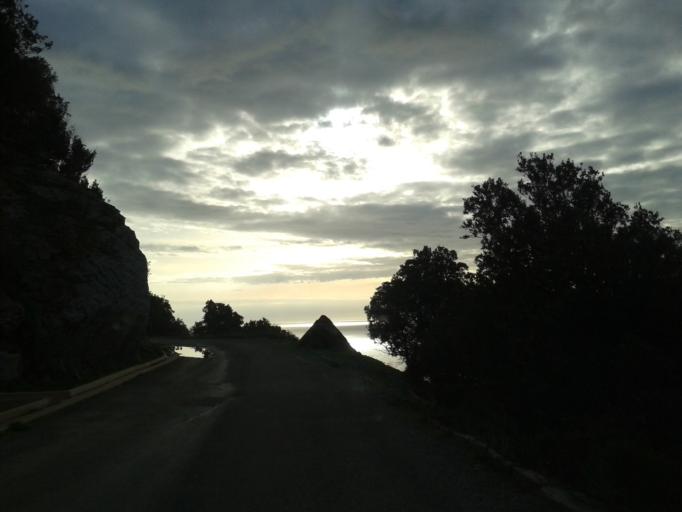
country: FR
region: Corsica
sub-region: Departement de la Haute-Corse
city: Brando
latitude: 42.9030
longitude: 9.3323
